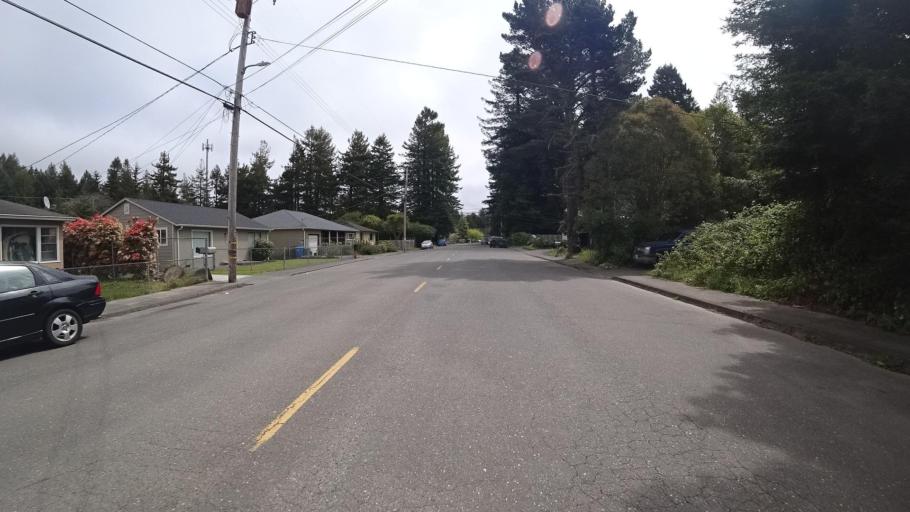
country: US
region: California
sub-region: Humboldt County
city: Cutten
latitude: 40.7698
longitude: -124.1406
